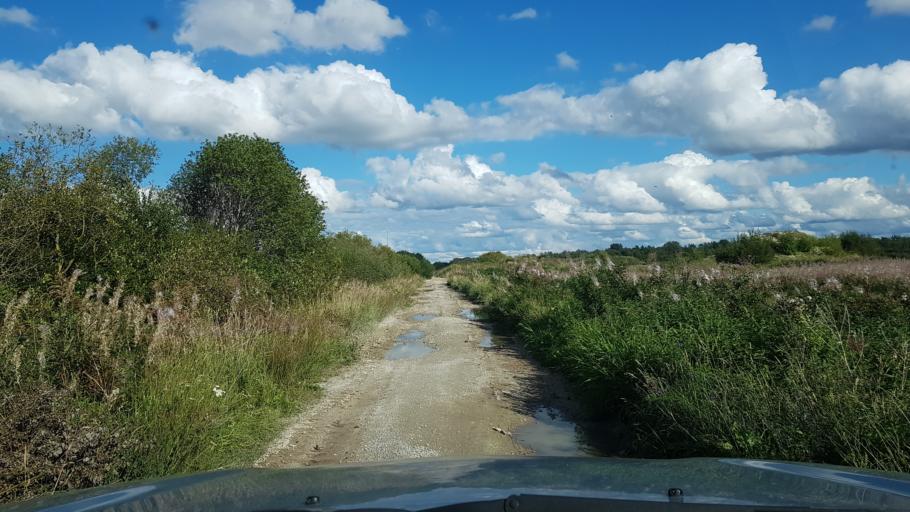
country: EE
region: Harju
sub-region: Kiili vald
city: Kiili
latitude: 59.3567
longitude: 24.8269
